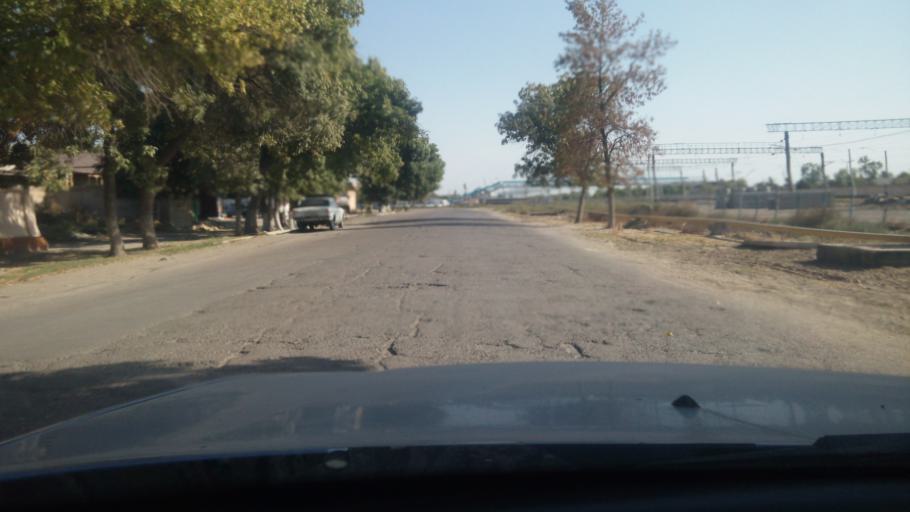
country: UZ
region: Sirdaryo
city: Guliston
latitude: 40.5013
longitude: 68.7638
